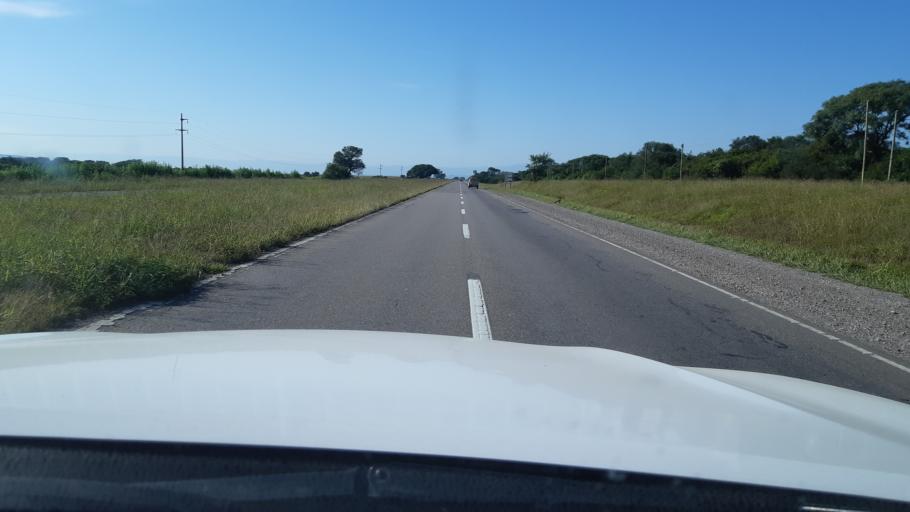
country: AR
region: Jujuy
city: Palpala
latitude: -24.3161
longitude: -65.1568
